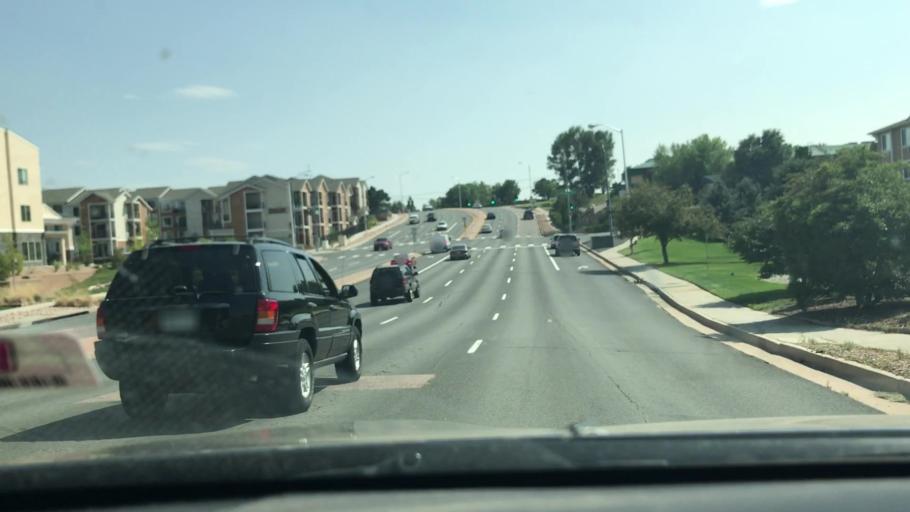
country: US
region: Colorado
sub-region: El Paso County
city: Colorado Springs
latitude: 38.9151
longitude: -104.7754
